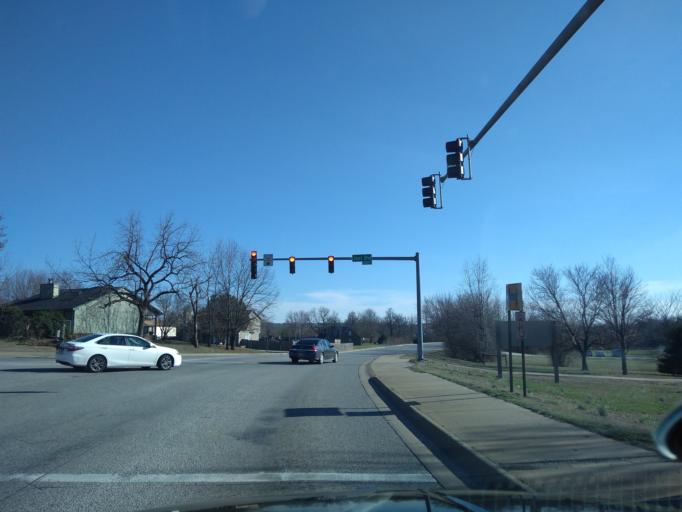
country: US
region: Arkansas
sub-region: Washington County
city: Johnson
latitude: 36.1255
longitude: -94.1624
